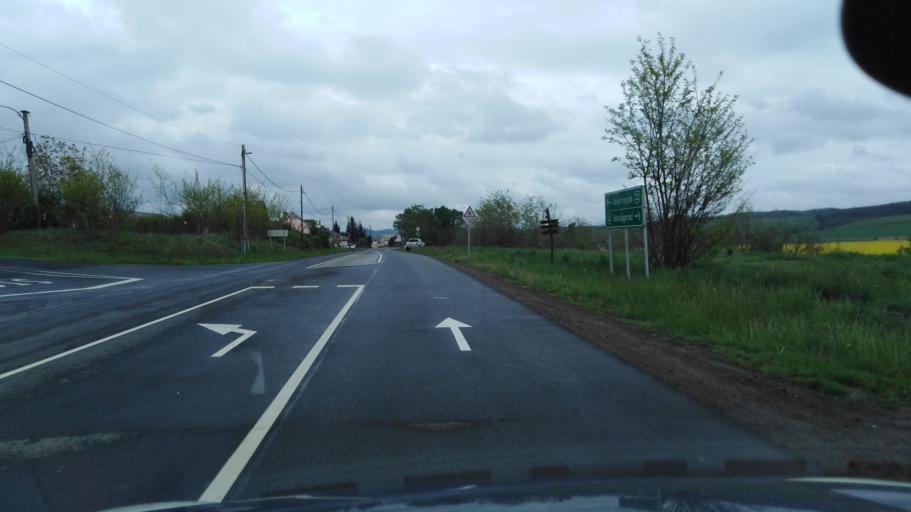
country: HU
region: Nograd
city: Szecseny
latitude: 48.1270
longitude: 19.5868
